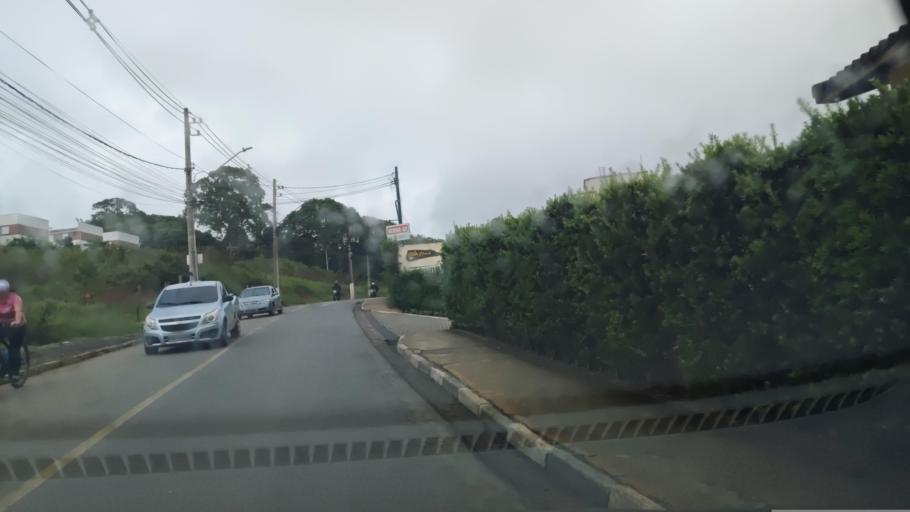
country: BR
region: Sao Paulo
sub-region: Vargem Grande Paulista
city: Vargem Grande Paulista
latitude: -23.6801
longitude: -47.0319
